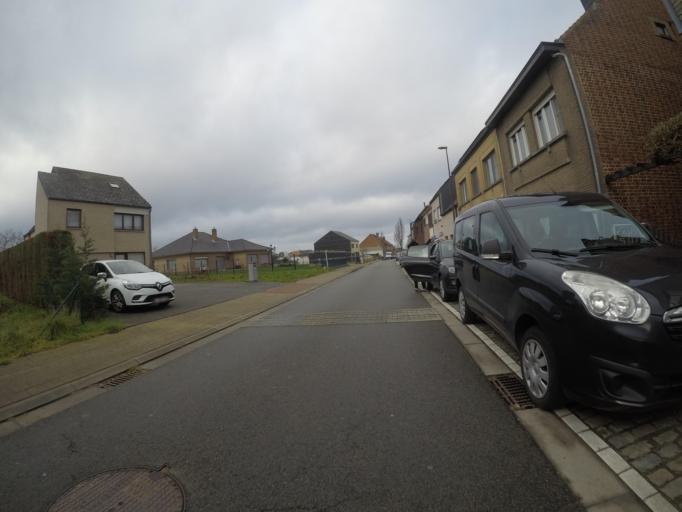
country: BE
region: Flanders
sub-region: Provincie Vlaams-Brabant
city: Liedekerke
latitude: 50.8663
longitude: 4.0927
